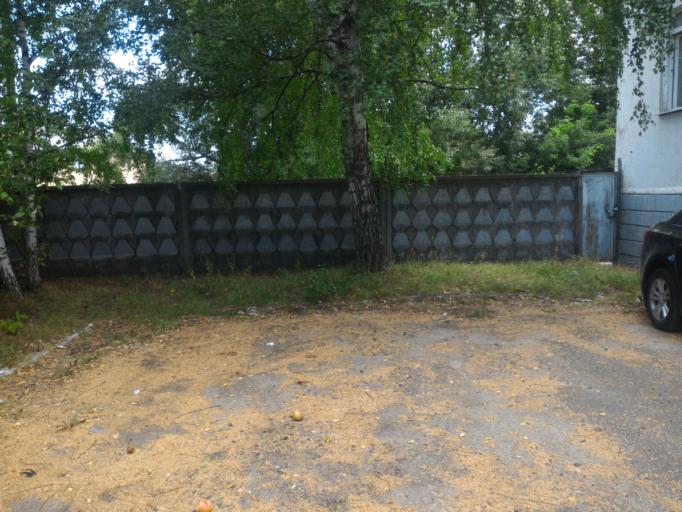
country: RU
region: Kursk
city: Kursk
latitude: 51.7329
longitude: 36.2359
